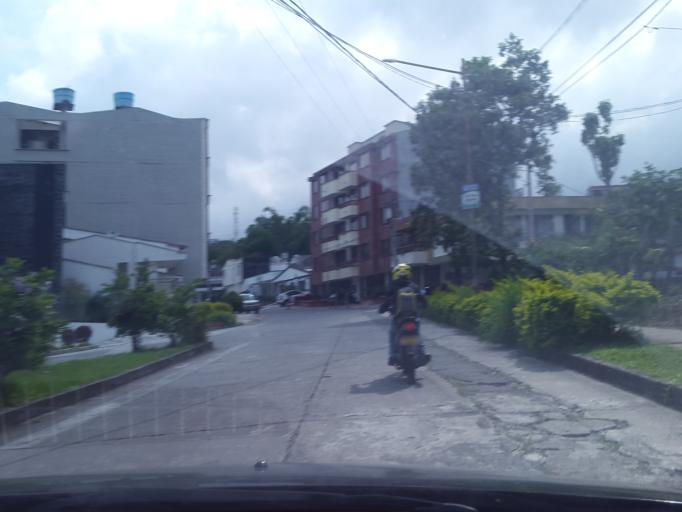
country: CO
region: Quindio
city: Armenia
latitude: 4.5485
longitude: -75.6656
